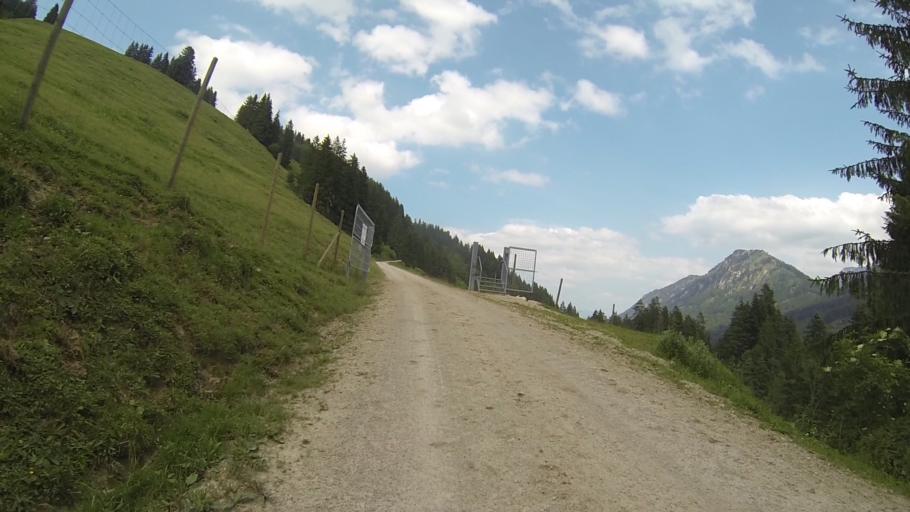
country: AT
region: Tyrol
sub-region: Politischer Bezirk Reutte
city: Jungholz
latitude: 47.5705
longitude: 10.4746
